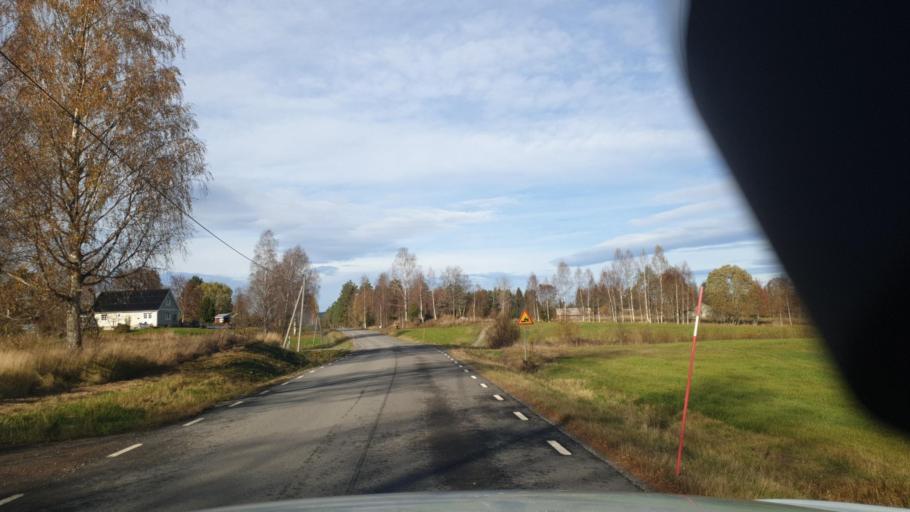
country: SE
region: Vaermland
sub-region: Eda Kommun
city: Charlottenberg
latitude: 59.9476
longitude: 12.5187
